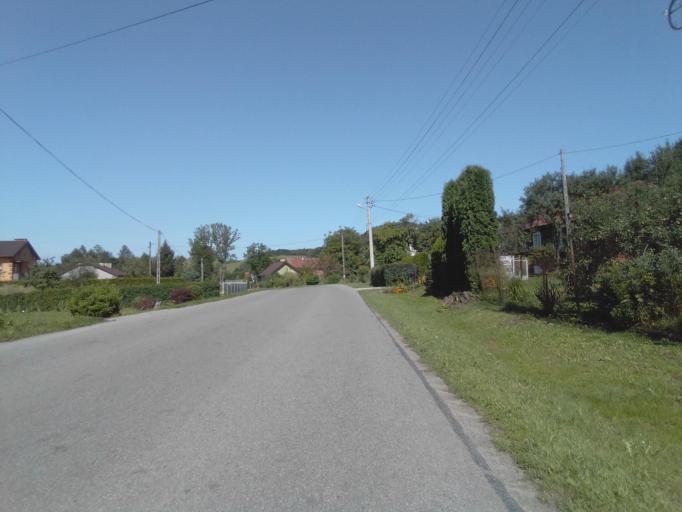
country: PL
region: Subcarpathian Voivodeship
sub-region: Powiat krosnienski
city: Chorkowka
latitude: 49.6101
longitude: 21.6231
